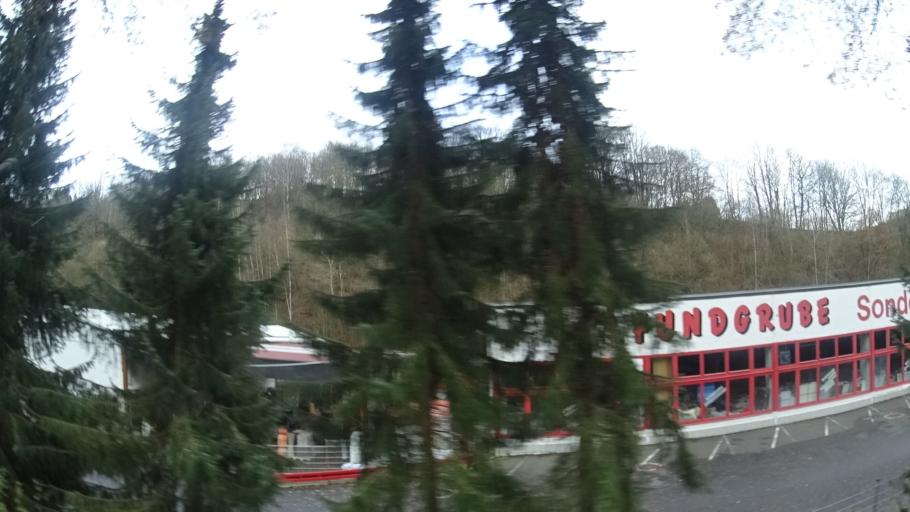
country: DE
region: Thuringia
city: Pappenheim
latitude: 50.7981
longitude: 10.4719
